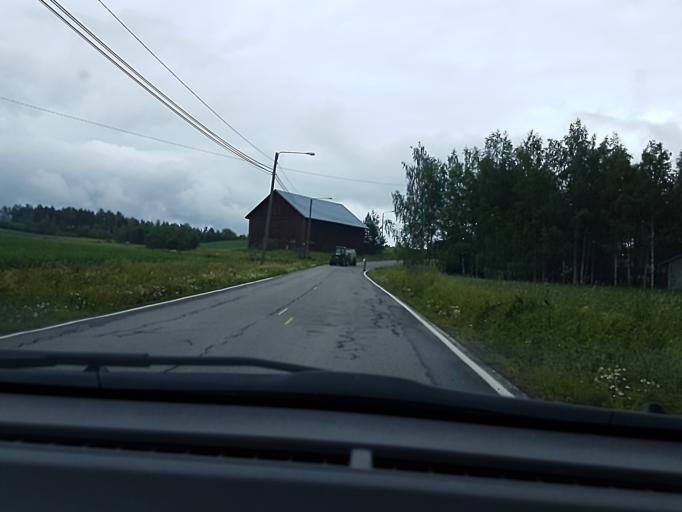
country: FI
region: Uusimaa
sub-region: Helsinki
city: Pornainen
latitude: 60.4342
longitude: 25.3908
